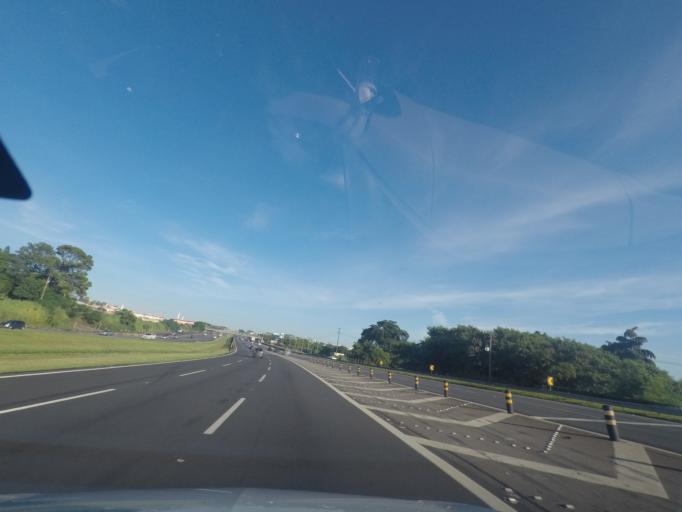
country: BR
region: Sao Paulo
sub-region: Campinas
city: Campinas
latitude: -22.8651
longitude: -47.1344
